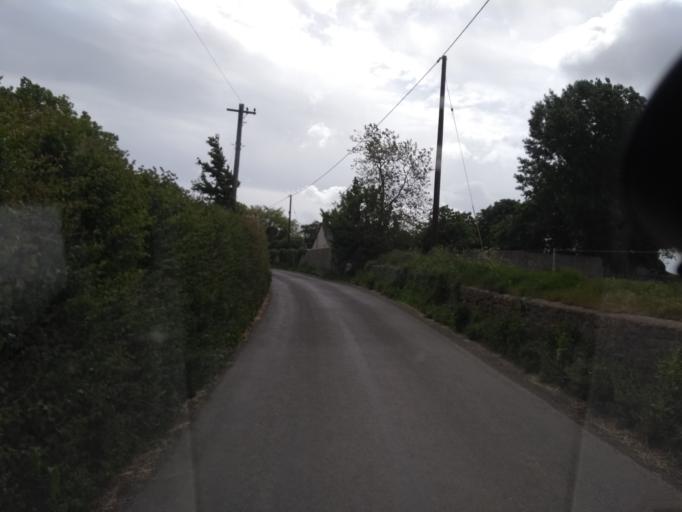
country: GB
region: England
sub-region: Somerset
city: Bishops Lydeard
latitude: 51.1814
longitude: -3.1515
